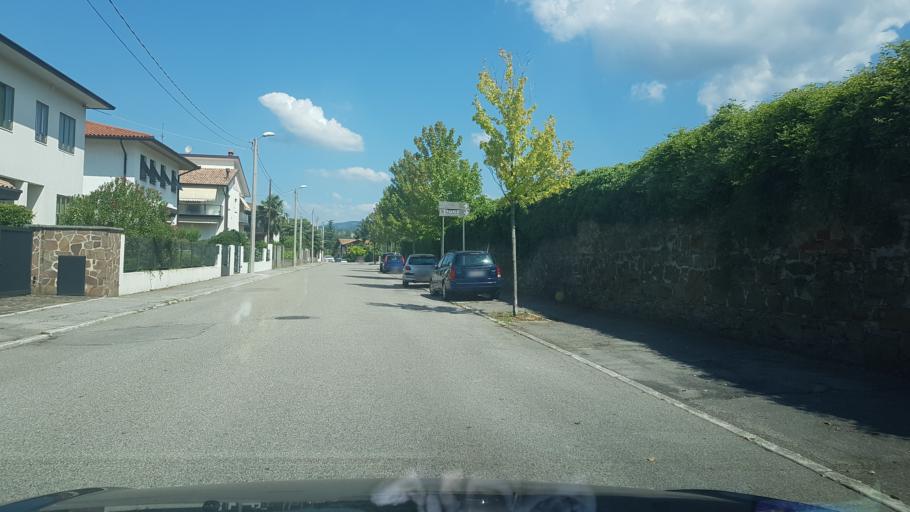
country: IT
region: Friuli Venezia Giulia
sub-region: Provincia di Gorizia
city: Gorizia
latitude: 45.9552
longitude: 13.6261
